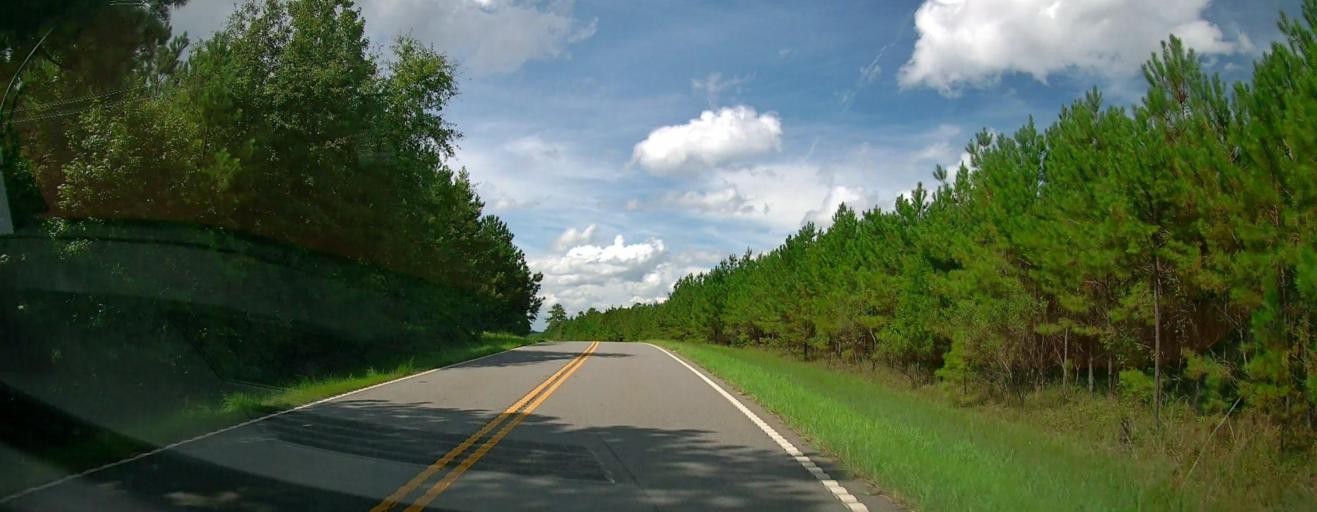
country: US
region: Georgia
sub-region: Talbot County
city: Talbotton
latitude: 32.6554
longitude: -84.5078
